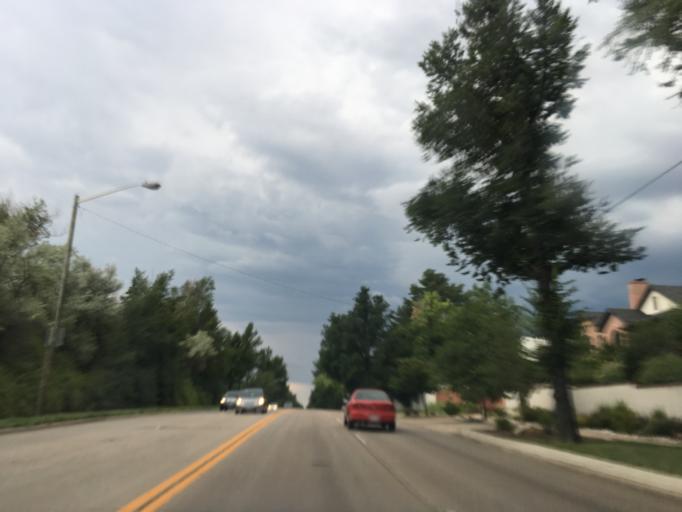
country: US
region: Colorado
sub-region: Arapahoe County
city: Glendale
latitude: 39.7104
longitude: -104.9594
